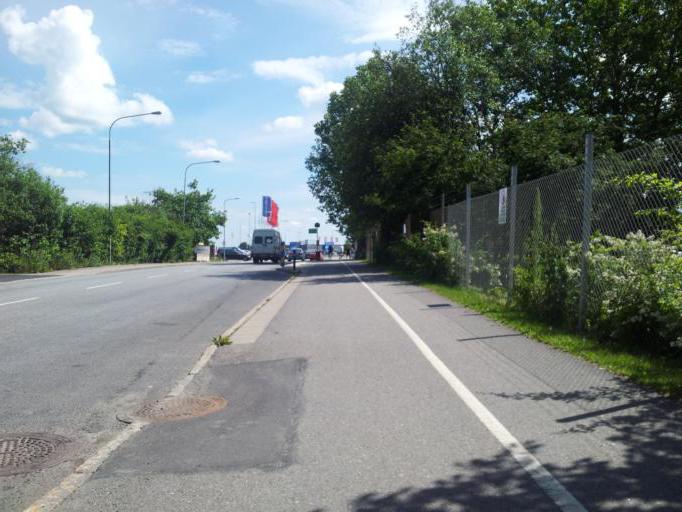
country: SE
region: Uppsala
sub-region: Uppsala Kommun
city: Saevja
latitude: 59.8536
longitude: 17.6802
